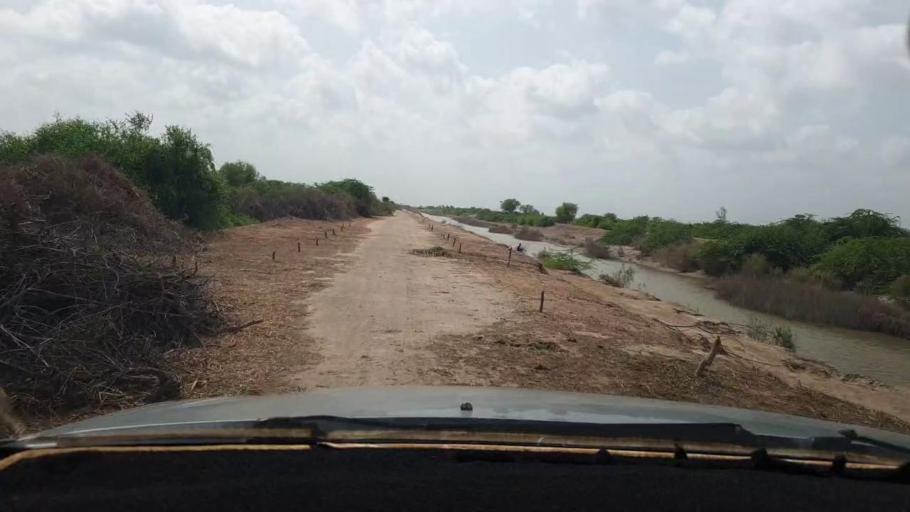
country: PK
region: Sindh
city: Tando Bago
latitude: 24.7240
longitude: 69.1353
